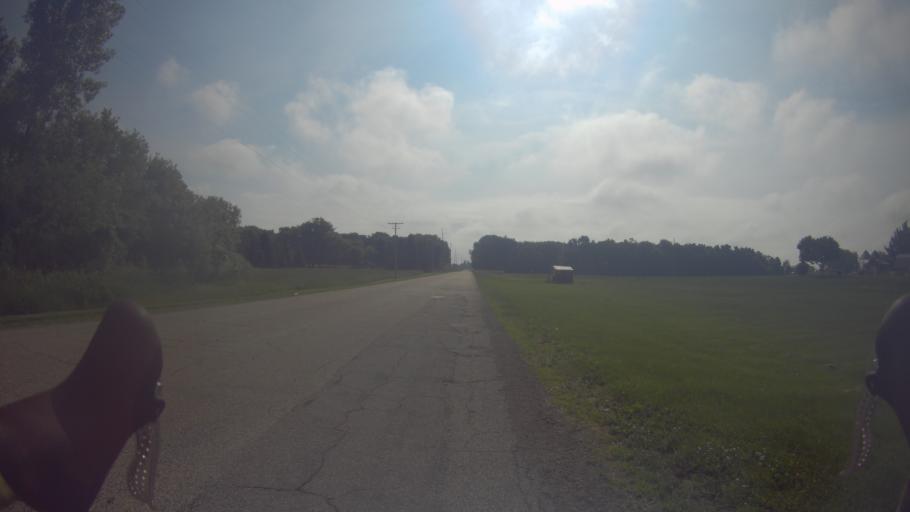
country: US
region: Wisconsin
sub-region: Dane County
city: McFarland
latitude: 42.9911
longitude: -89.2275
